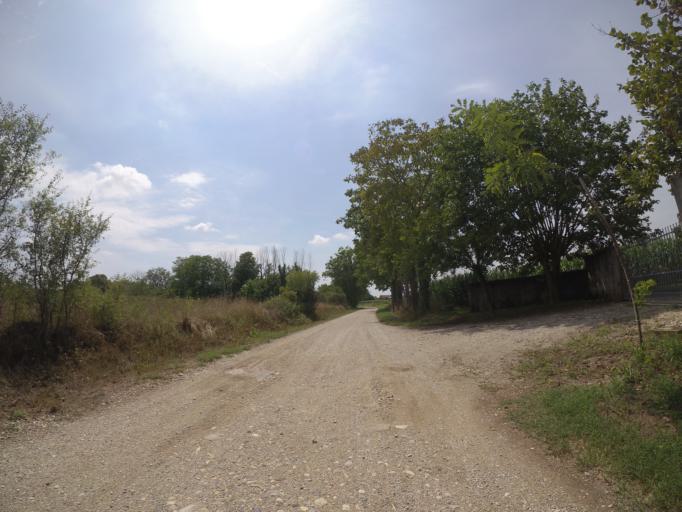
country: IT
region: Friuli Venezia Giulia
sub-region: Provincia di Udine
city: Lestizza
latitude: 45.9636
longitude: 13.1160
